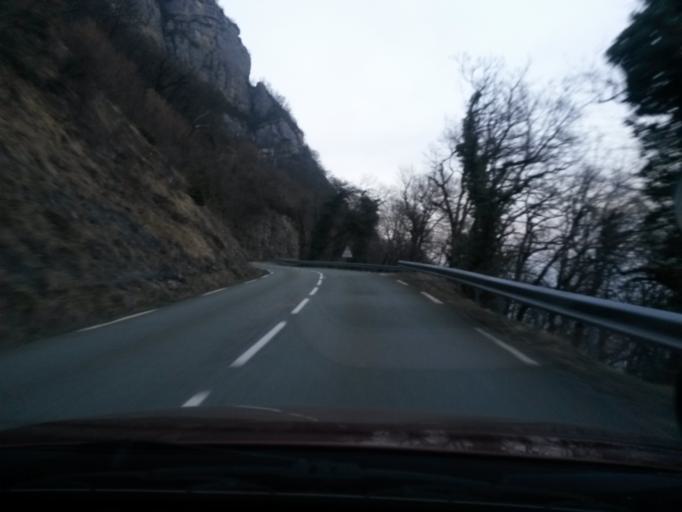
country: FR
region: Rhone-Alpes
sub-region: Departement de l'Isere
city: Bernin
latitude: 45.2781
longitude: 5.8420
